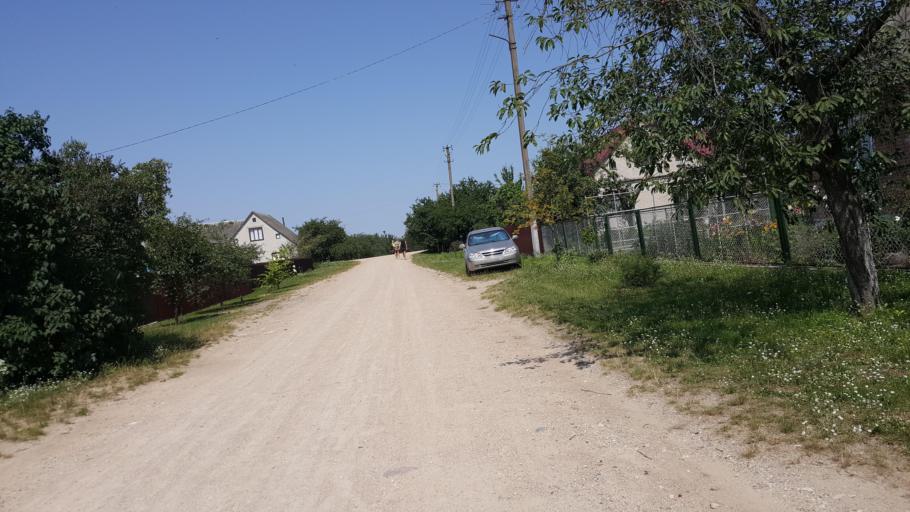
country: BY
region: Brest
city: Zhabinka
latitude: 52.1953
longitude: 23.9819
